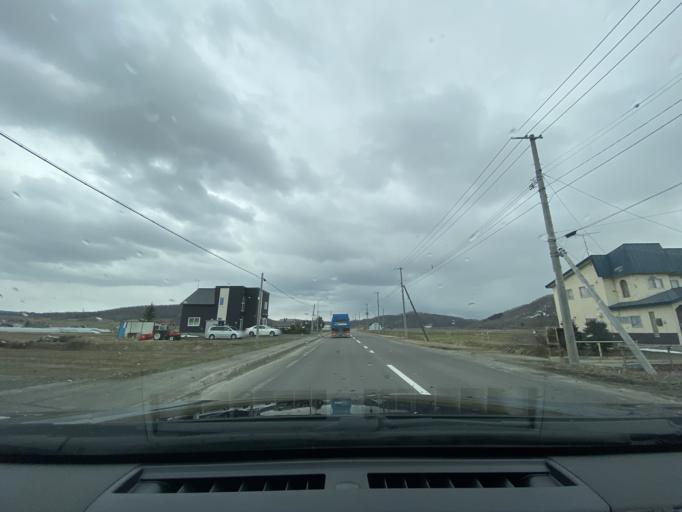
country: JP
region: Hokkaido
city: Nayoro
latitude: 44.1793
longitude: 142.2813
